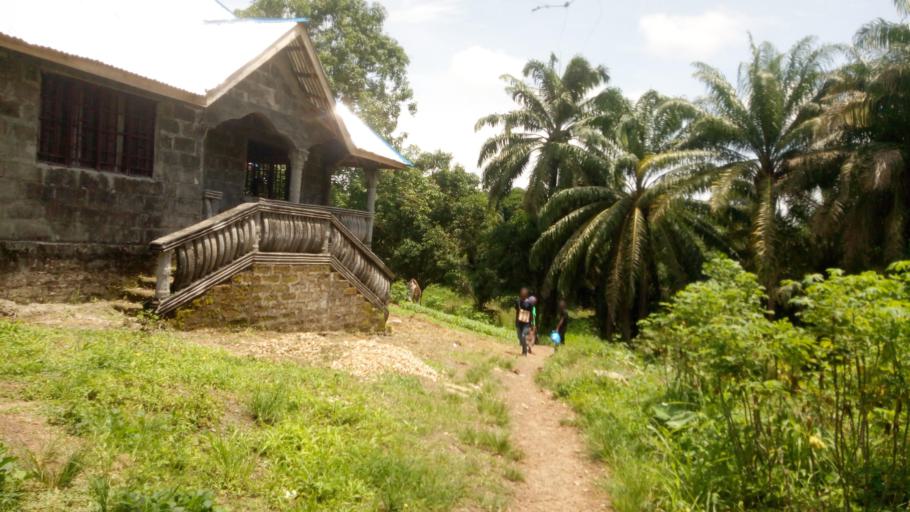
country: SL
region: Northern Province
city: Magburaka
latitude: 8.7194
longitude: -11.9586
